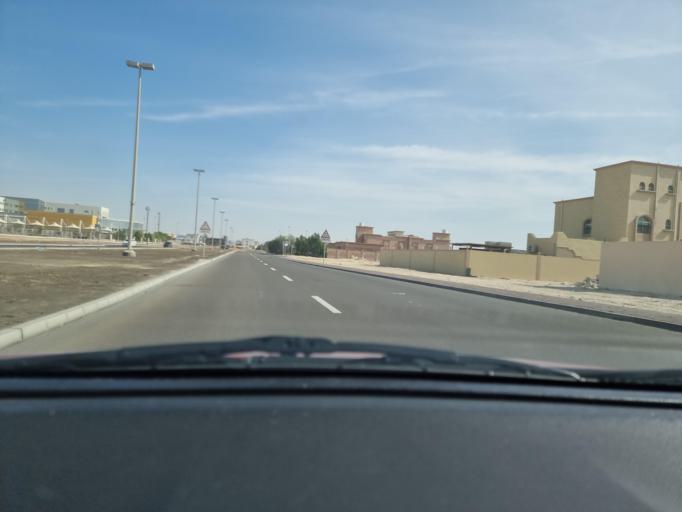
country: AE
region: Abu Dhabi
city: Abu Dhabi
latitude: 24.3125
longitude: 54.5562
